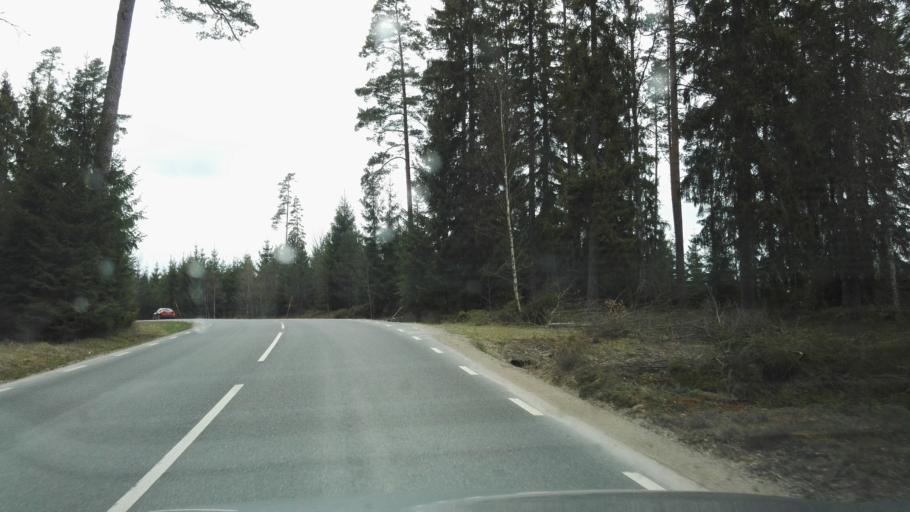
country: SE
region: Kronoberg
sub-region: Vaxjo Kommun
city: Braas
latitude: 57.1851
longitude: 14.9639
